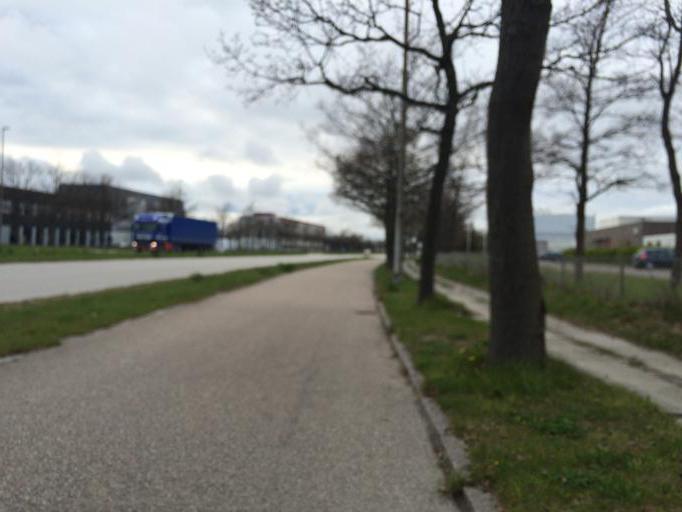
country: DK
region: Capital Region
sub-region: Hvidovre Kommune
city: Hvidovre
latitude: 55.6132
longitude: 12.4590
